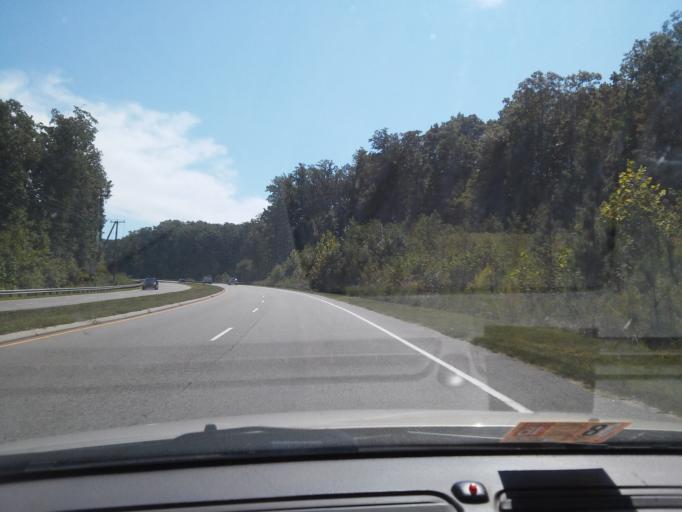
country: US
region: Virginia
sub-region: Chesterfield County
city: Bon Air
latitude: 37.5447
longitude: -77.6520
